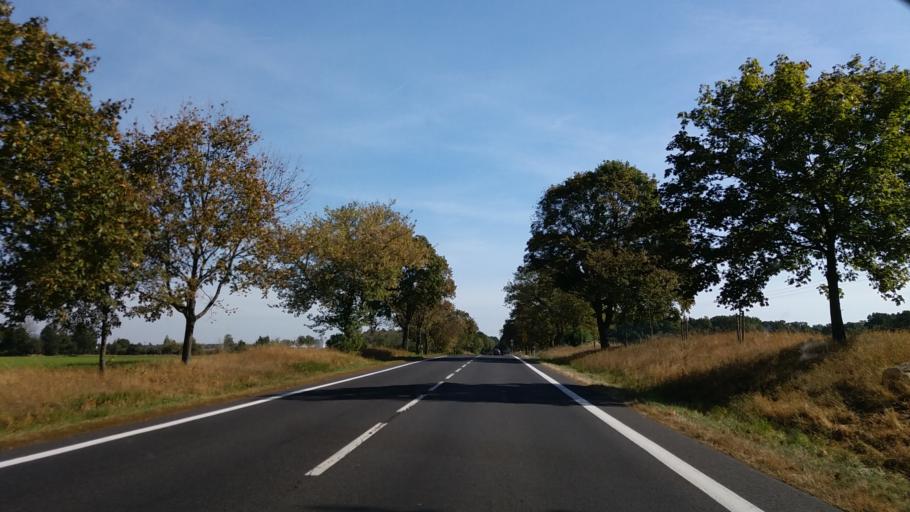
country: PL
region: Greater Poland Voivodeship
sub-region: Powiat miedzychodzki
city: Kwilcz
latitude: 52.5453
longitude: 16.1202
